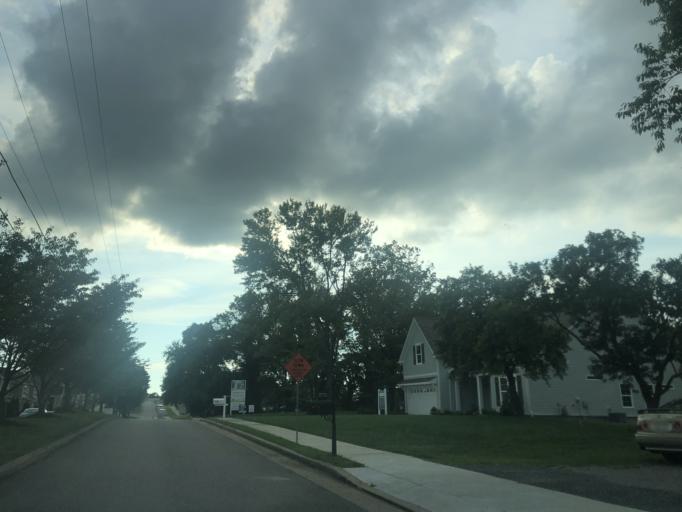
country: US
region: Tennessee
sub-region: Davidson County
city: Lakewood
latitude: 36.1703
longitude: -86.6189
